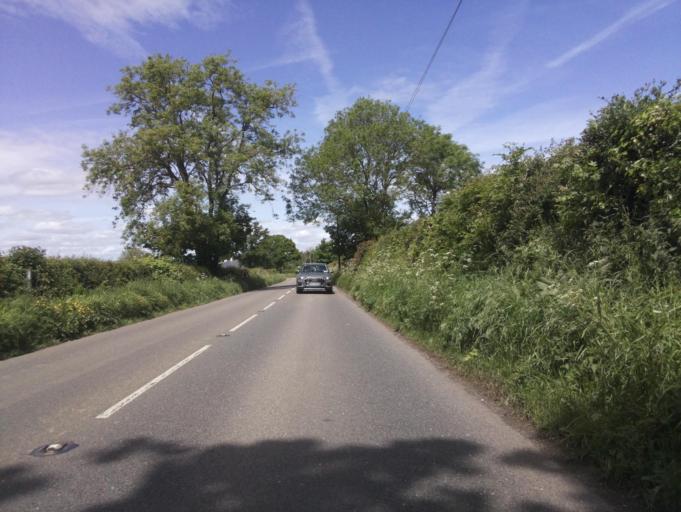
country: GB
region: England
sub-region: Devon
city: Uffculme
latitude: 50.8428
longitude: -3.3177
